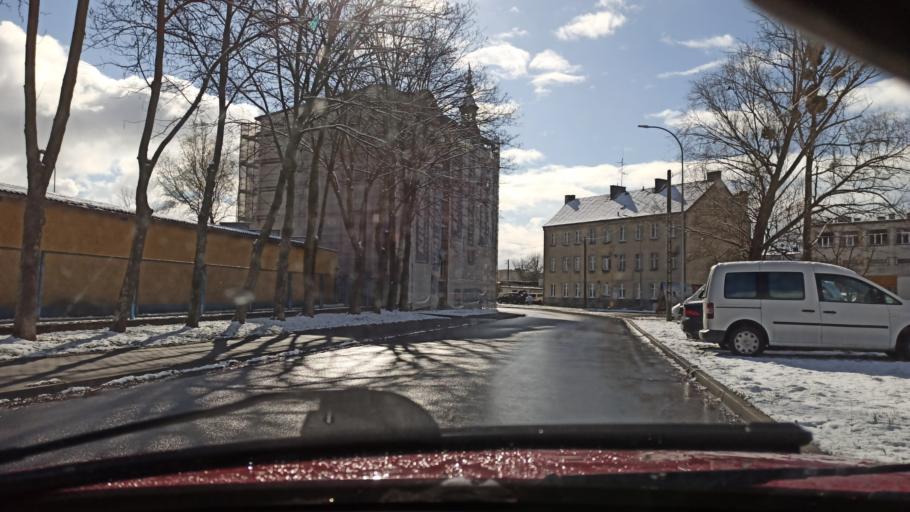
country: PL
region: Warmian-Masurian Voivodeship
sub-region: Powiat elblaski
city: Elblag
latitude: 54.1536
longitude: 19.3951
